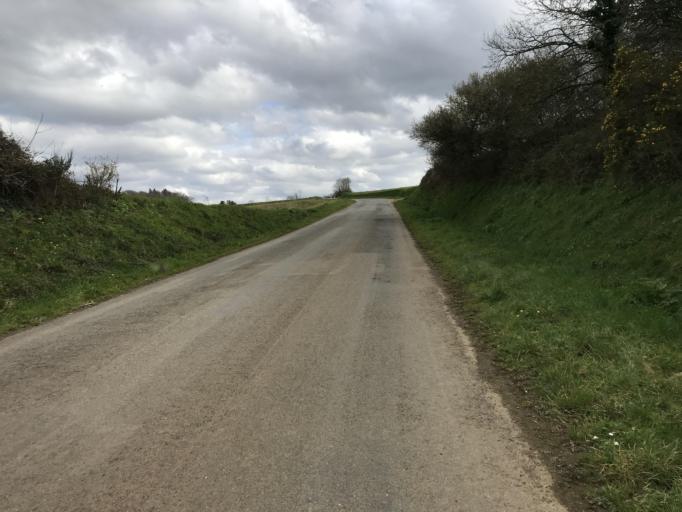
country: FR
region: Brittany
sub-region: Departement du Finistere
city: Hopital-Camfrout
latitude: 48.3210
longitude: -4.2196
